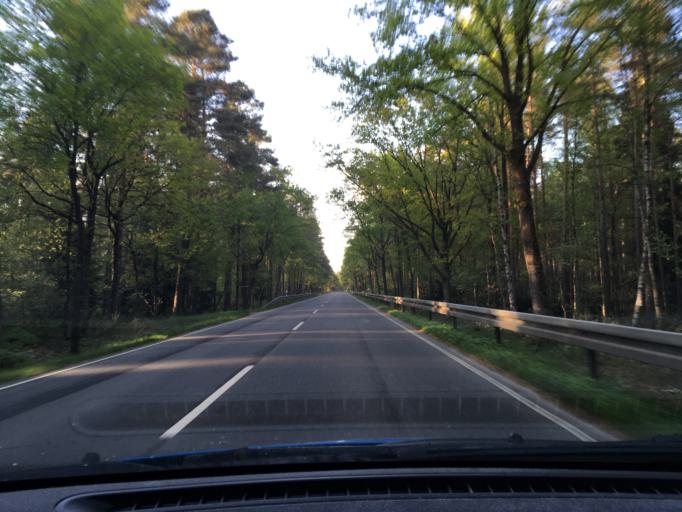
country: DE
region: Lower Saxony
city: Wietzendorf
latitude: 52.8671
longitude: 9.9810
